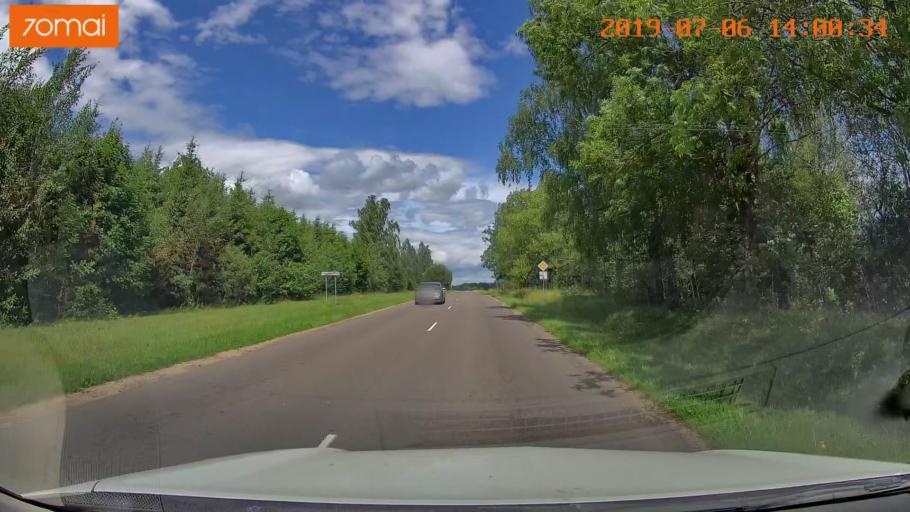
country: BY
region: Minsk
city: Ivyanyets
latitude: 53.8005
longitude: 26.8184
